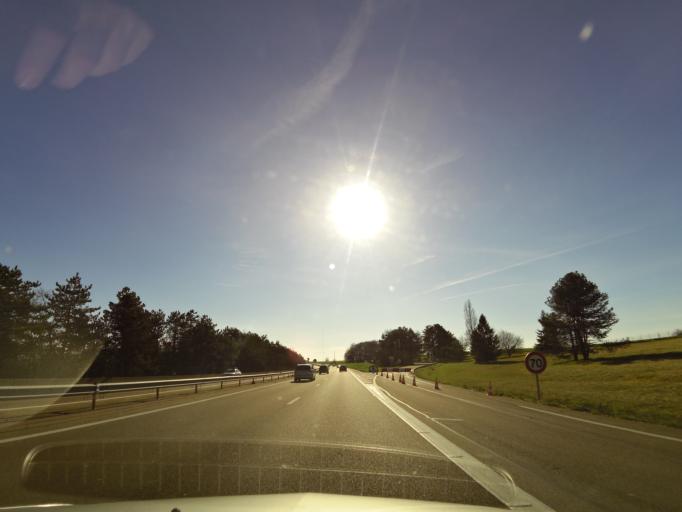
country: FR
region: Bourgogne
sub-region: Departement de l'Yonne
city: Saint-Bris-le-Vineux
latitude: 47.7543
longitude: 3.7280
